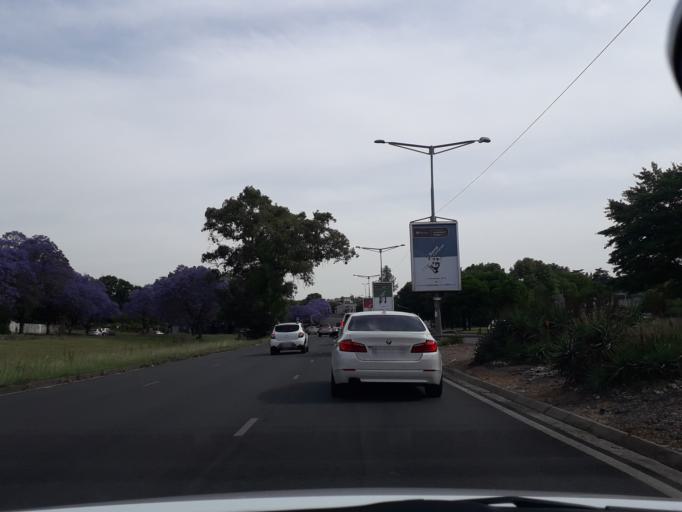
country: ZA
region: Gauteng
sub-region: City of Johannesburg Metropolitan Municipality
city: Johannesburg
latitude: -26.1050
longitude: 28.0322
